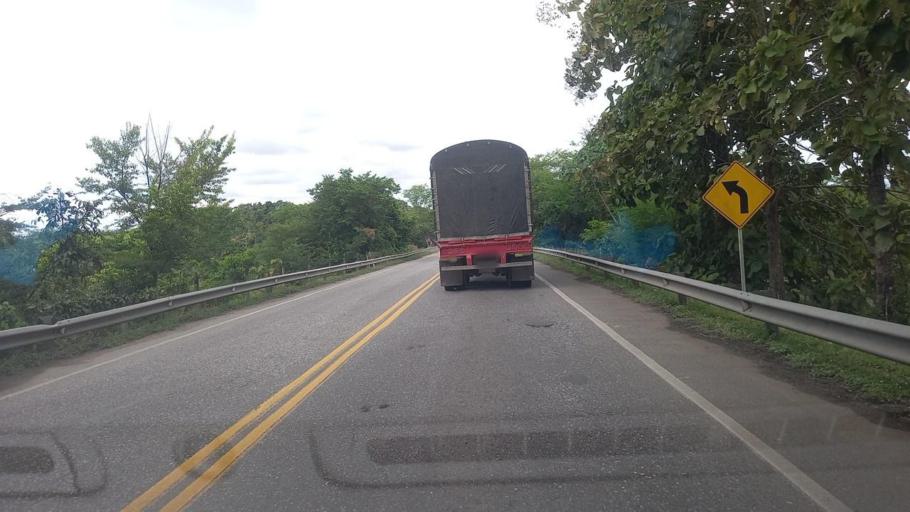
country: CO
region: Antioquia
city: Puerto Triunfo
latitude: 5.8743
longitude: -74.5674
